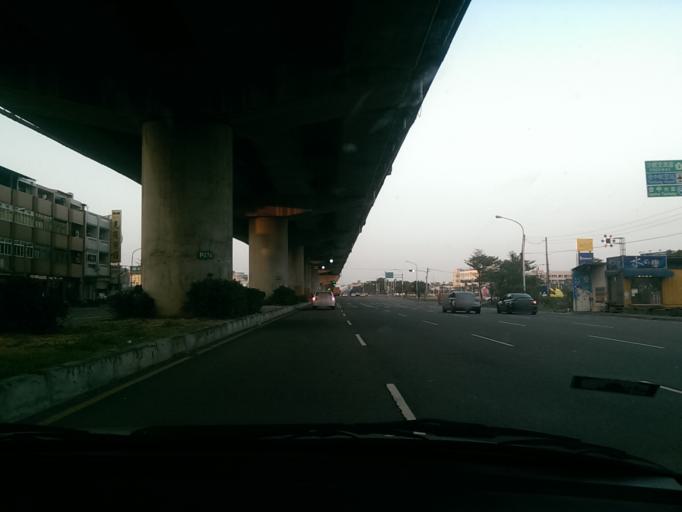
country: TW
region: Taiwan
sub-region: Changhua
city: Chang-hua
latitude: 24.2471
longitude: 120.5352
